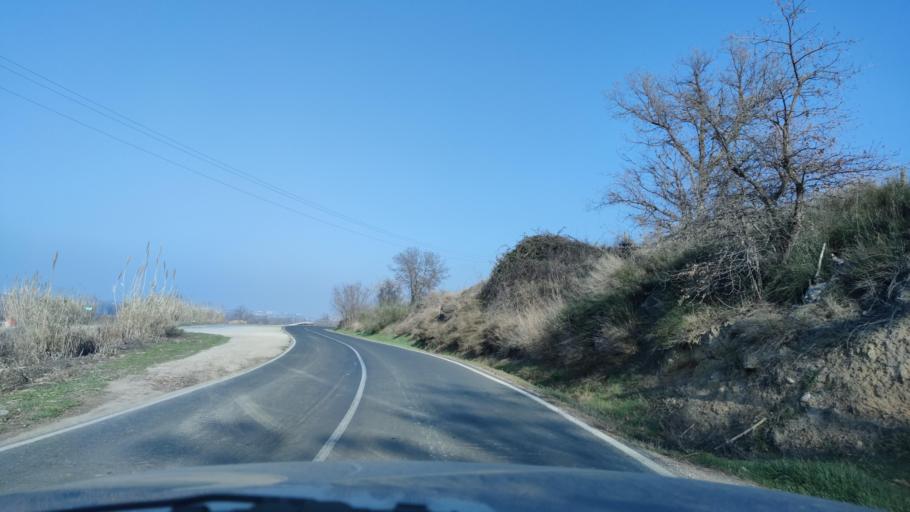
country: ES
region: Catalonia
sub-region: Provincia de Lleida
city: Sunyer
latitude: 41.5600
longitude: 0.5748
